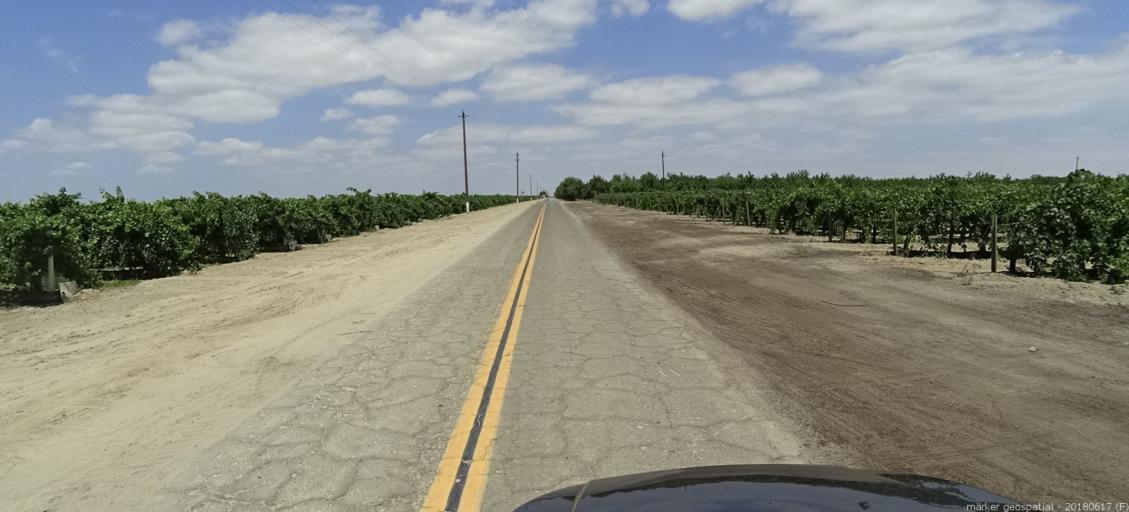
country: US
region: California
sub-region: Fresno County
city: Biola
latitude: 36.8228
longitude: -120.0969
